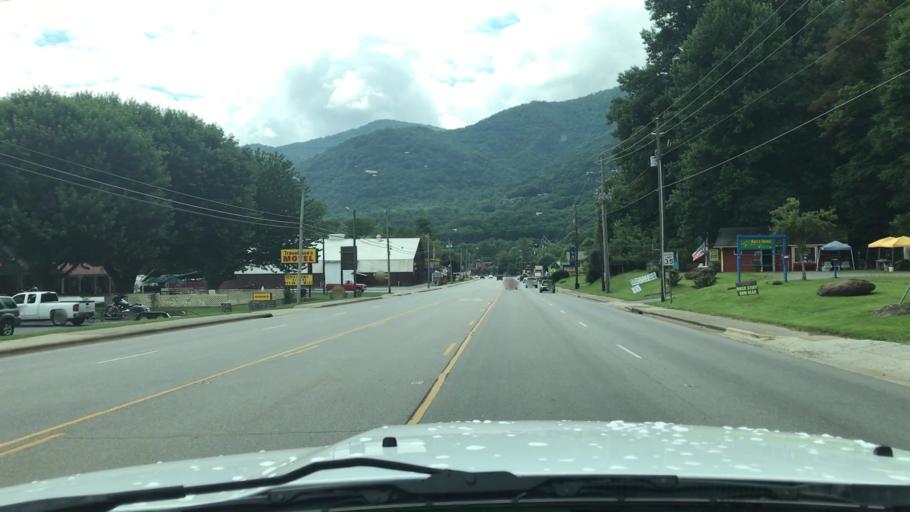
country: US
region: North Carolina
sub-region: Haywood County
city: Maggie Valley
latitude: 35.5146
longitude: -83.0826
